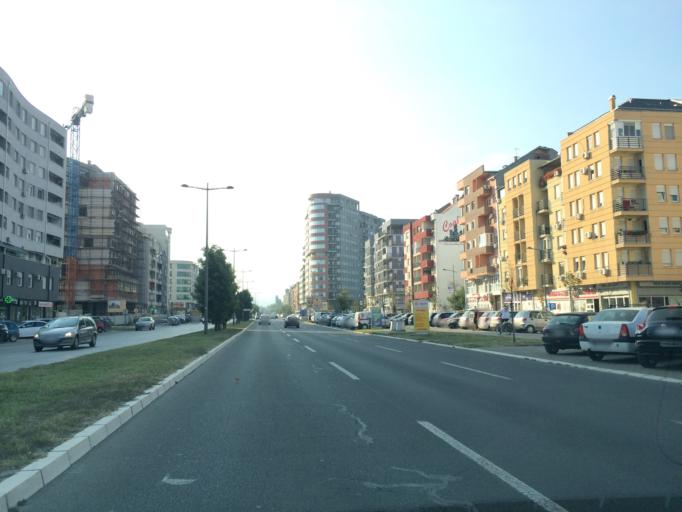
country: RS
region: Autonomna Pokrajina Vojvodina
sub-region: Juznobacki Okrug
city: Novi Sad
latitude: 45.2454
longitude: 19.8187
